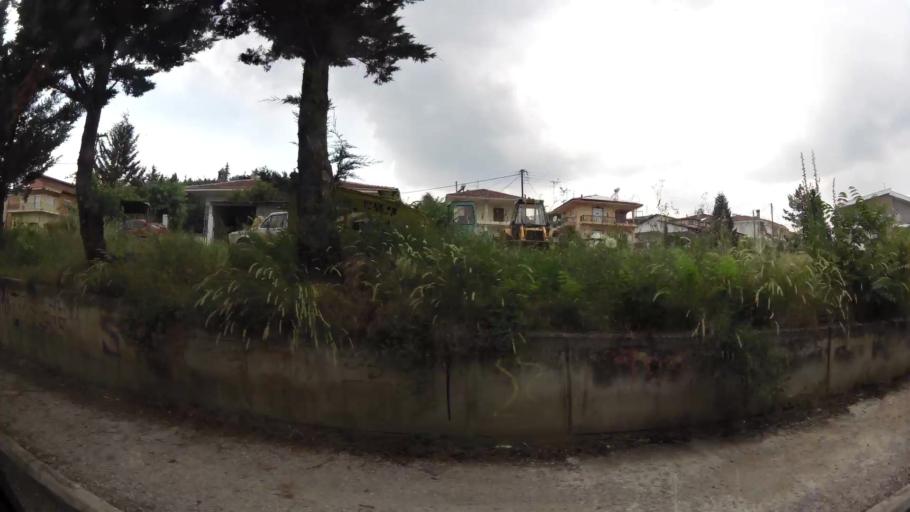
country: GR
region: West Macedonia
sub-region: Nomos Kozanis
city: Koila
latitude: 40.3255
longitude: 21.8264
